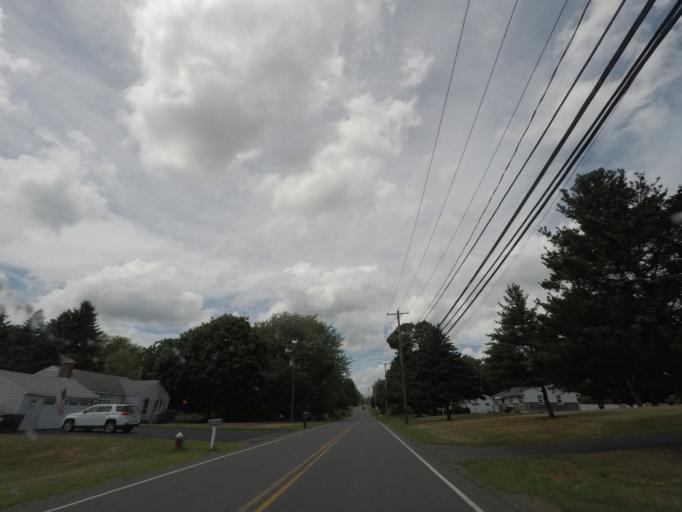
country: US
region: New York
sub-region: Rensselaer County
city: Wynantskill
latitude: 42.7078
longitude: -73.6250
